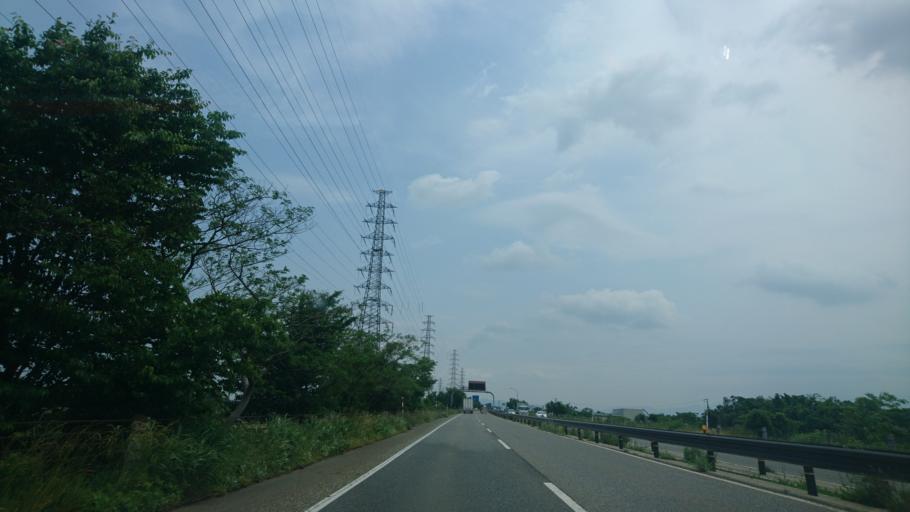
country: JP
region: Niigata
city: Suibara
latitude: 37.9492
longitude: 139.2015
